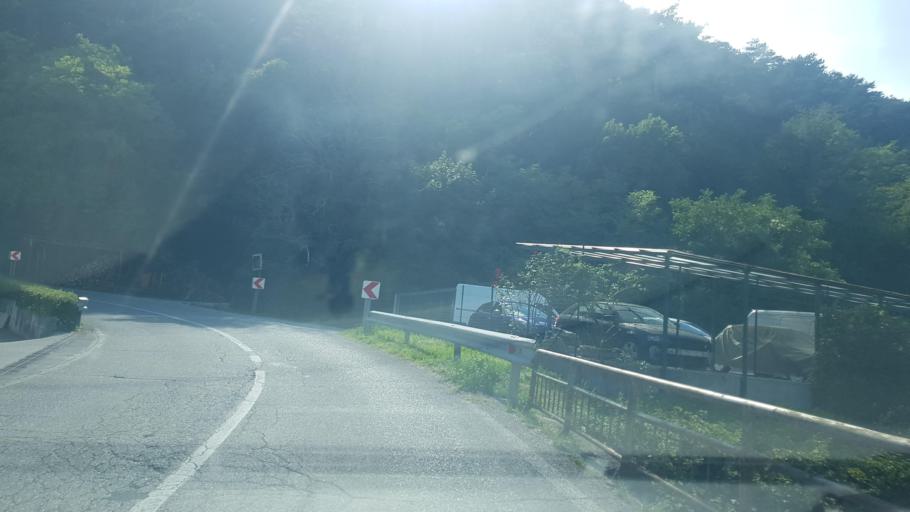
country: SI
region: Komen
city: Komen
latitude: 45.8513
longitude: 13.8041
